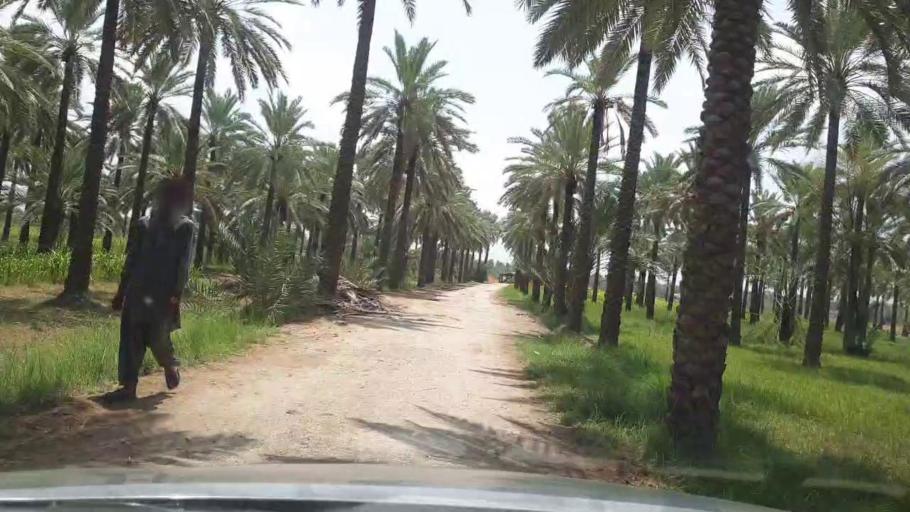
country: PK
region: Sindh
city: Khairpur
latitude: 27.6327
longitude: 68.7334
